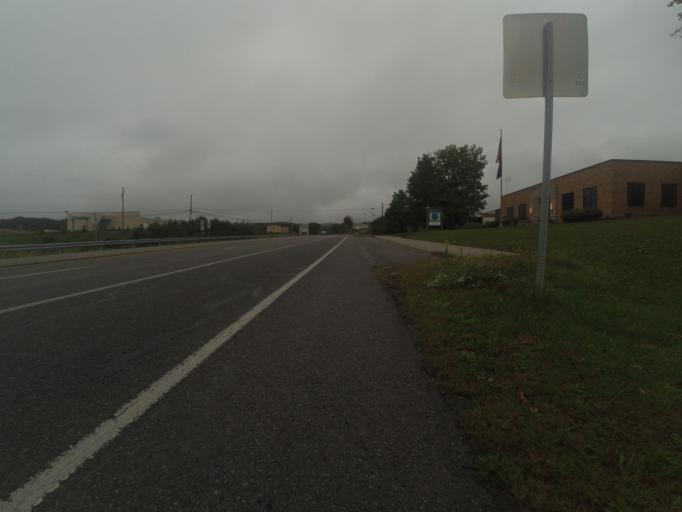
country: US
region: Pennsylvania
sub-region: Huntingdon County
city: Huntingdon
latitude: 40.4925
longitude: -78.0405
